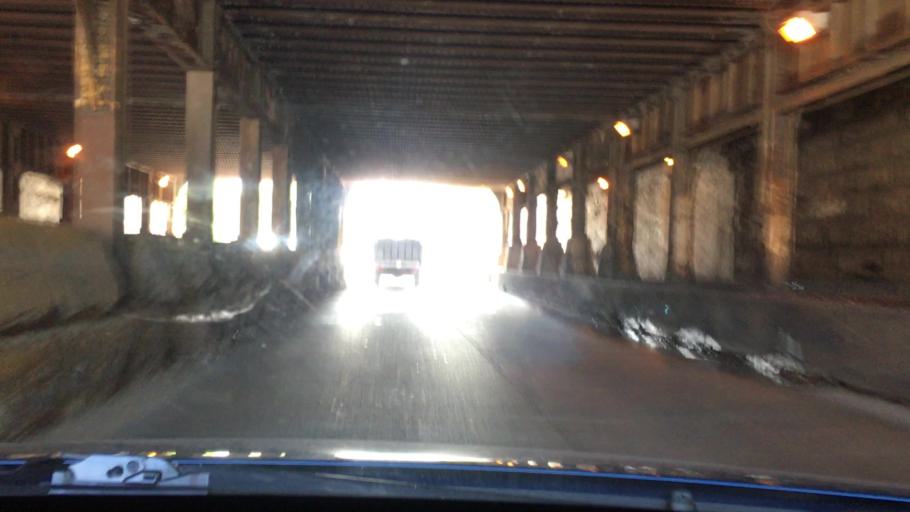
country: US
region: Illinois
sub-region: Cook County
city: Chicago
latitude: 41.8886
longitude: -87.6867
